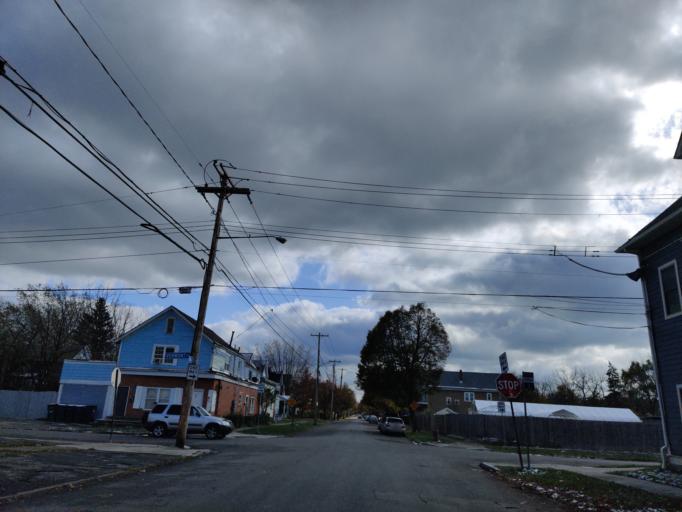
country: US
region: New York
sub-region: Erie County
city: Buffalo
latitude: 42.9076
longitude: -78.8896
